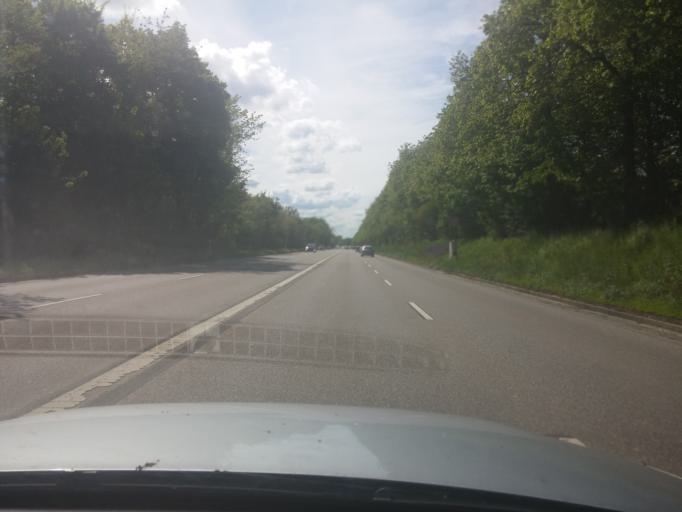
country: DE
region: Bavaria
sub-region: Upper Bavaria
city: Neubiberg
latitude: 48.1059
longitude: 11.6291
